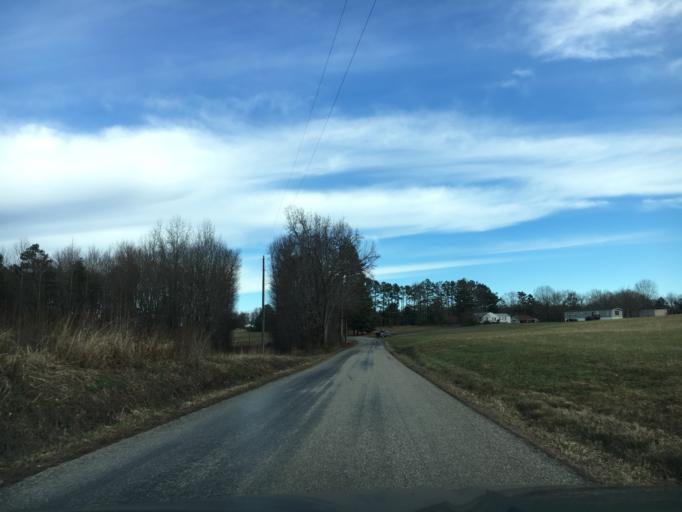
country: US
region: Virginia
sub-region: Nottoway County
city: Crewe
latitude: 37.2399
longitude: -78.2307
